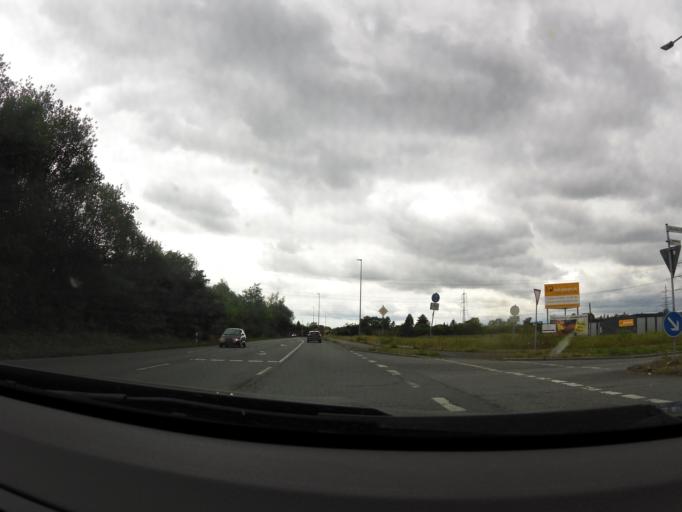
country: DE
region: North Rhine-Westphalia
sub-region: Regierungsbezirk Dusseldorf
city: Voerde
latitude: 51.6297
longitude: 6.6912
